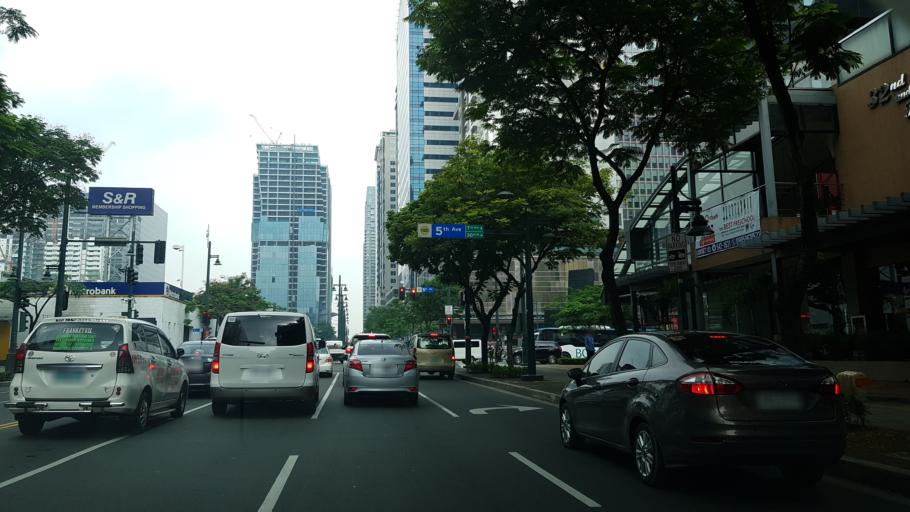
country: PH
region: Metro Manila
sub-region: Makati City
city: Makati City
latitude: 14.5544
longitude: 121.0480
